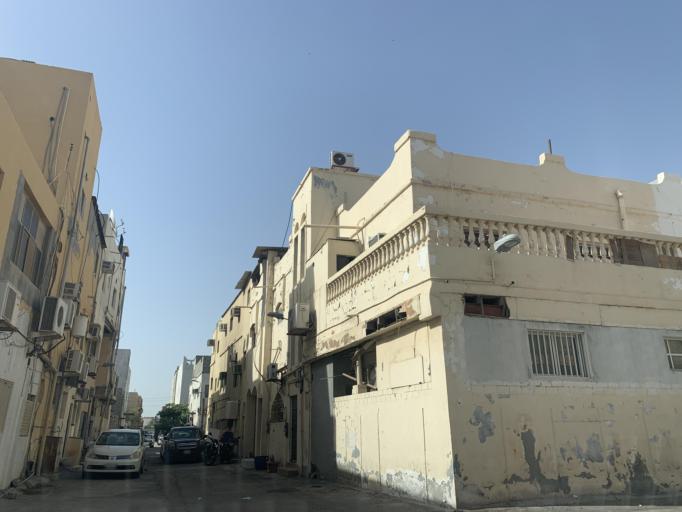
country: BH
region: Northern
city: Sitrah
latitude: 26.1643
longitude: 50.6112
